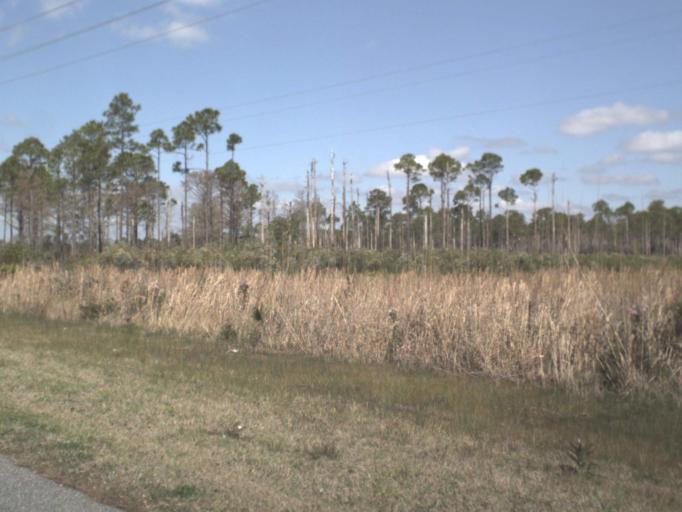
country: US
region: Florida
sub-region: Franklin County
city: Apalachicola
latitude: 29.7243
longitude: -85.0776
